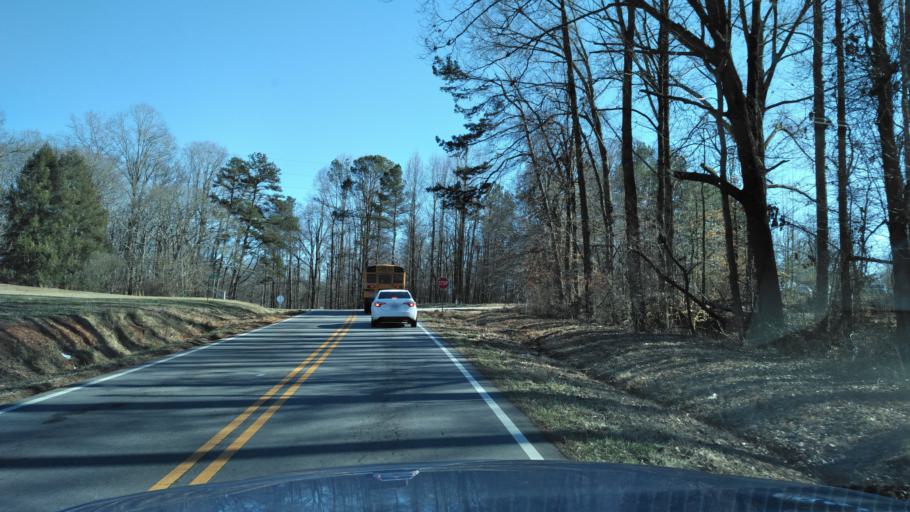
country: US
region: Georgia
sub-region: Hall County
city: Gainesville
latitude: 34.3101
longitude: -83.7412
